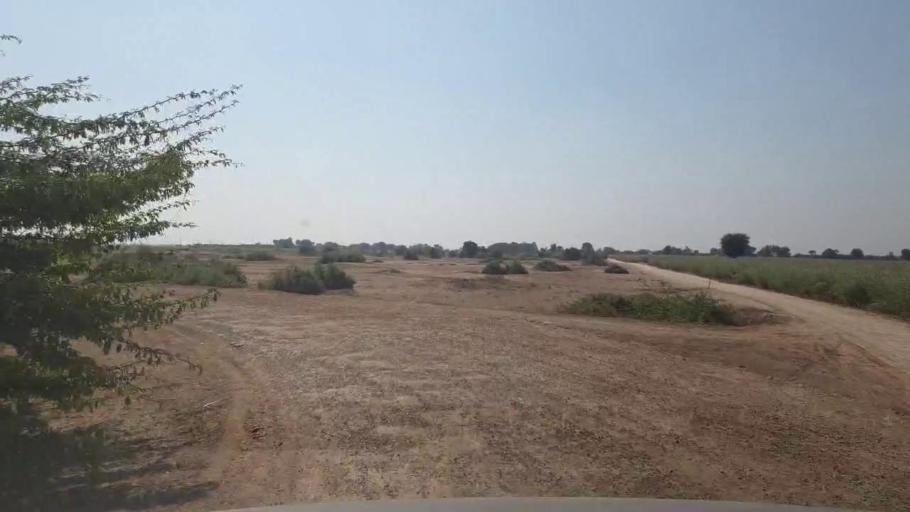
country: PK
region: Sindh
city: Digri
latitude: 25.2297
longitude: 69.2207
